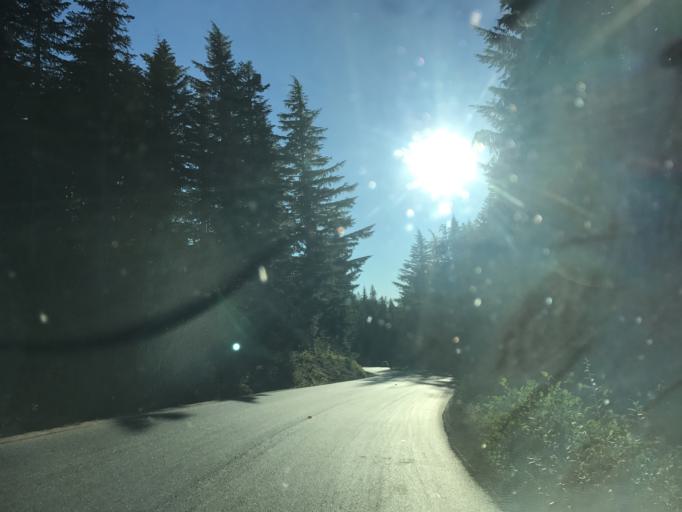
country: US
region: Washington
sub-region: Pierce County
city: Buckley
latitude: 46.7699
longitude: -121.7710
